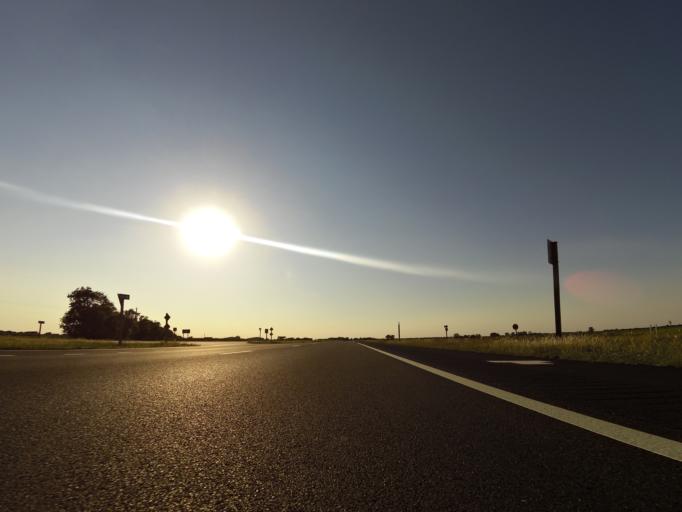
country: US
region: Kansas
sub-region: Reno County
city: Haven
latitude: 37.8764
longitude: -97.7015
